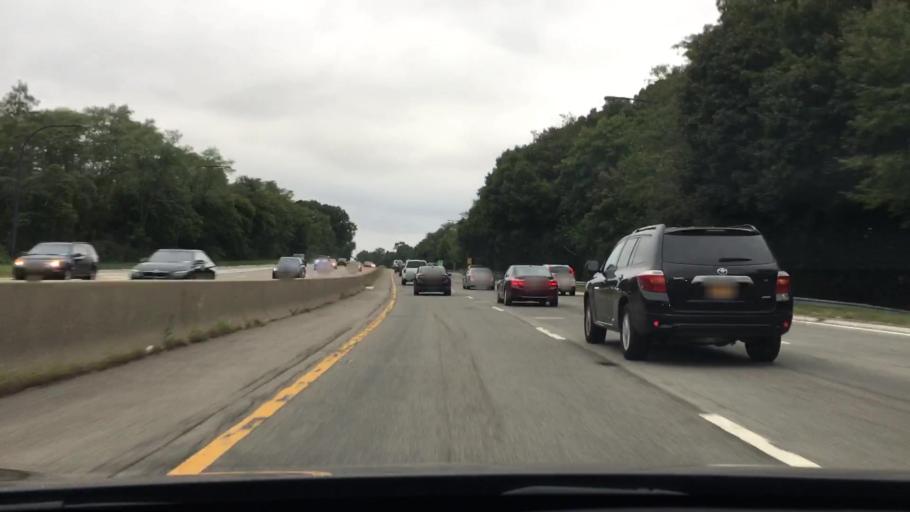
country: US
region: New York
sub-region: Nassau County
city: Roslyn Heights
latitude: 40.7819
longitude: -73.6467
